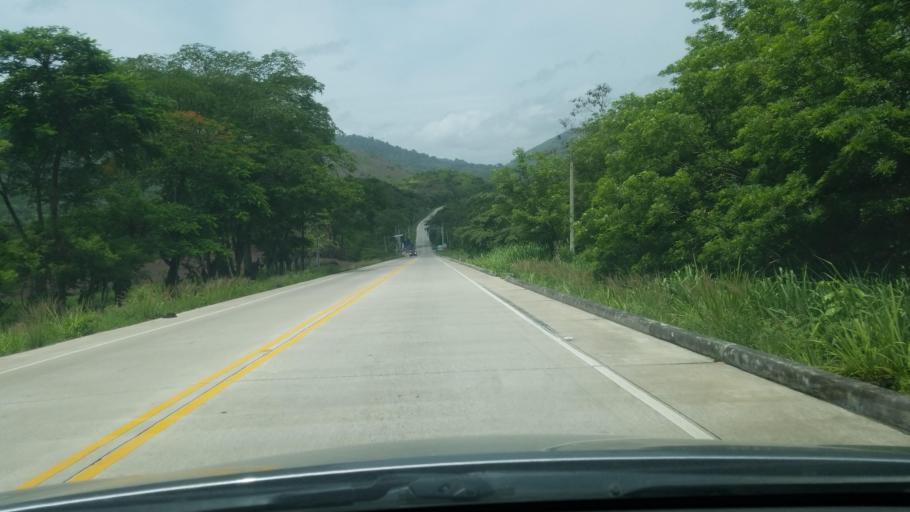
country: HN
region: Copan
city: Quezailica
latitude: 14.8947
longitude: -88.7600
